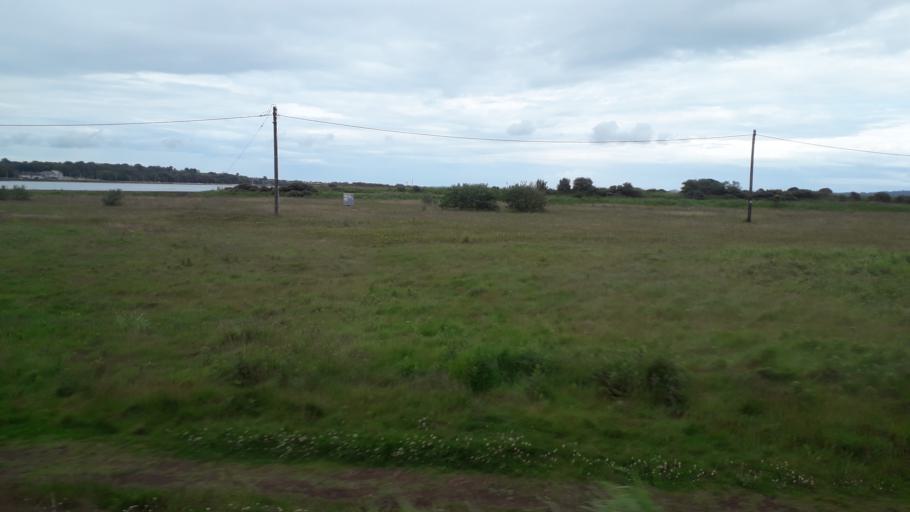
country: IE
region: Leinster
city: Dollymount
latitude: 53.3575
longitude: -6.1756
